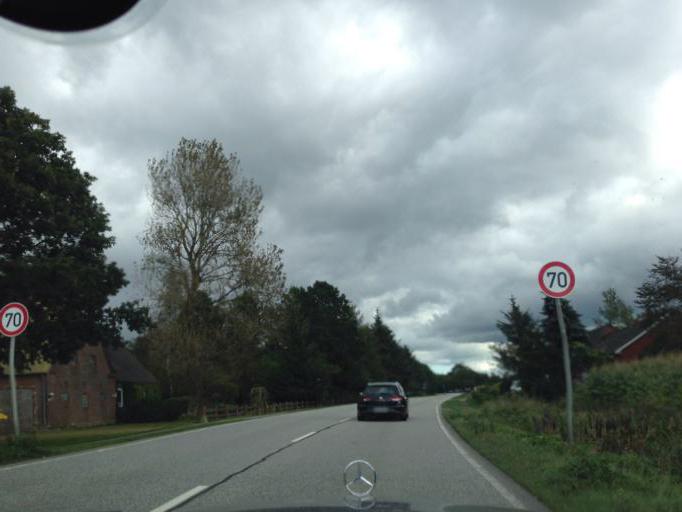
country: DE
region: Schleswig-Holstein
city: Stadum
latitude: 54.7443
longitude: 9.0402
